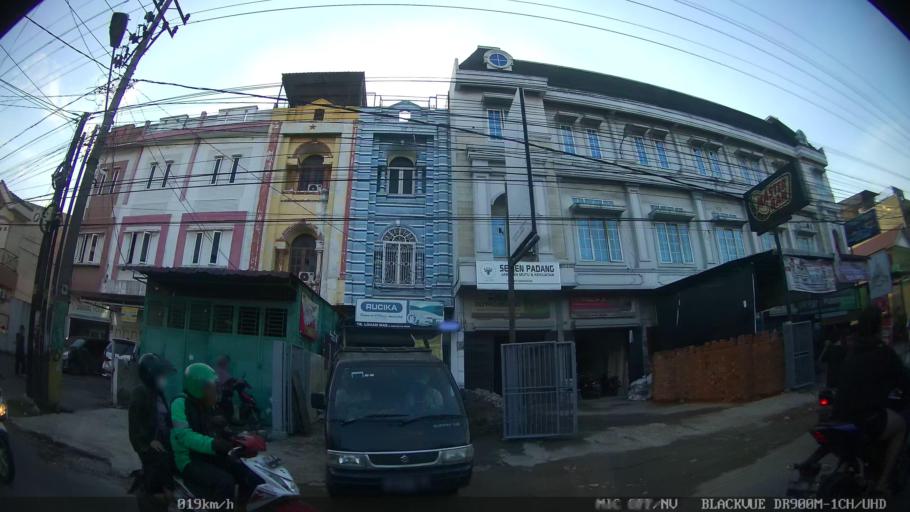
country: ID
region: North Sumatra
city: Medan
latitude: 3.6111
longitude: 98.6655
